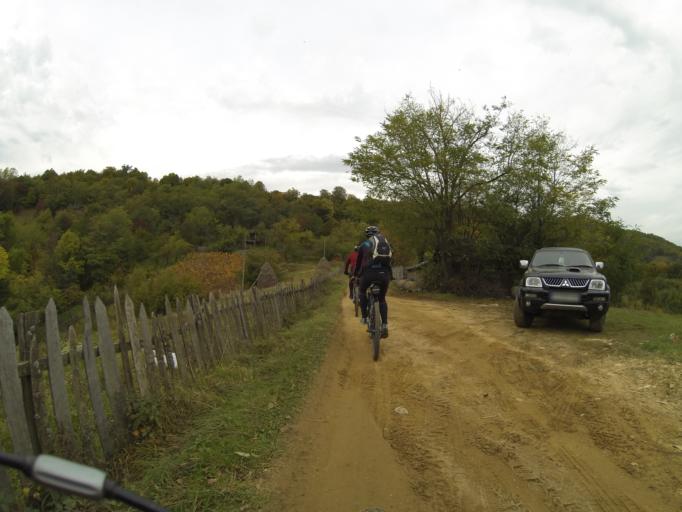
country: RO
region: Gorj
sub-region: Comuna Tismana
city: Sohodol
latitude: 45.0642
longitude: 22.8710
